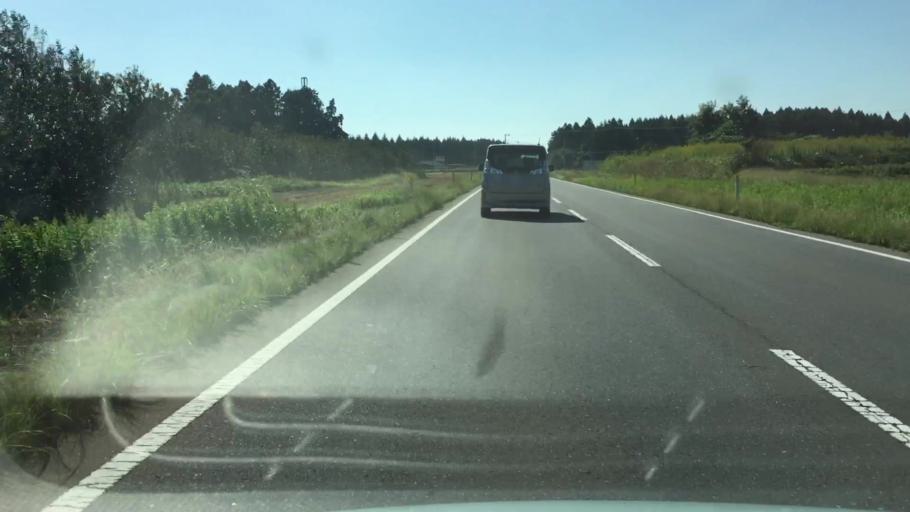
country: JP
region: Ibaraki
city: Ami
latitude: 35.9866
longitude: 140.1853
